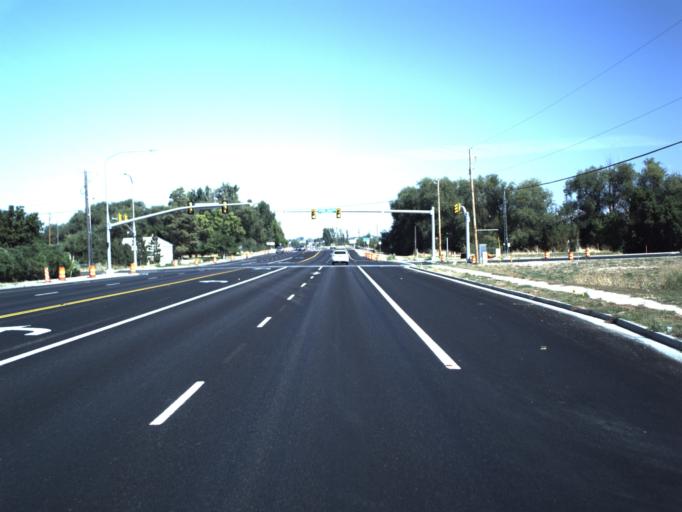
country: US
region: Utah
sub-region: Cache County
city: Nibley
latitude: 41.6845
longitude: -111.8337
